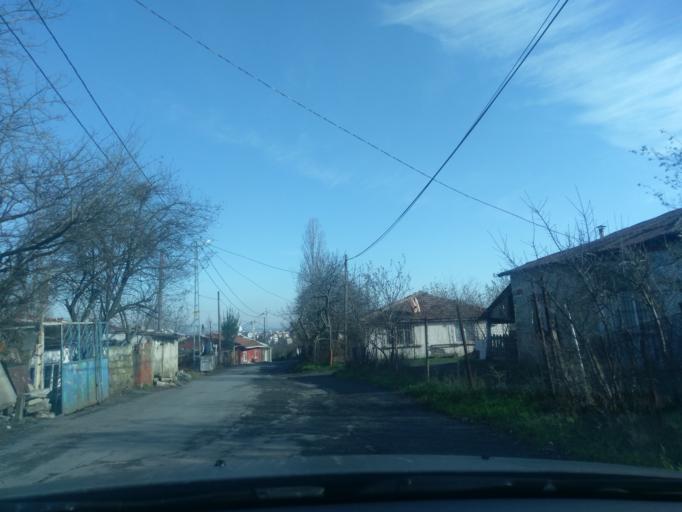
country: TR
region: Istanbul
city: Sultangazi
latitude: 41.1369
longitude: 28.8463
